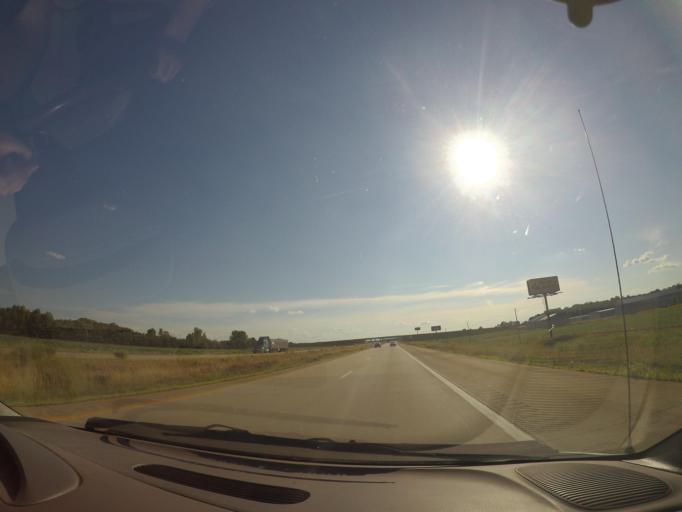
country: US
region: Ohio
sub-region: Lucas County
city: Whitehouse
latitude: 41.4355
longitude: -83.8681
